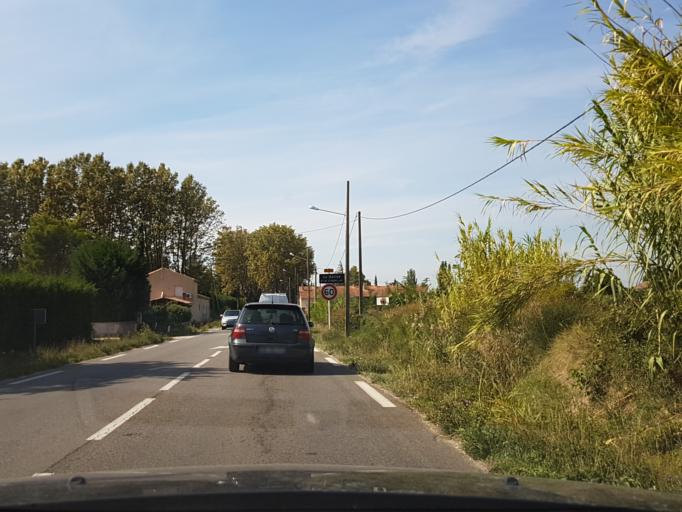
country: FR
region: Provence-Alpes-Cote d'Azur
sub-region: Departement des Bouches-du-Rhone
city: Saint-Remy-de-Provence
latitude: 43.7850
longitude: 4.8682
